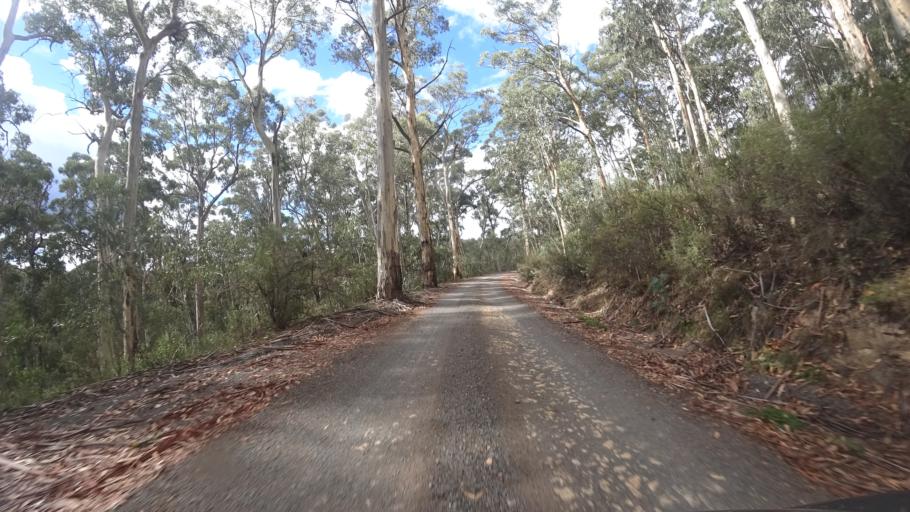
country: AU
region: New South Wales
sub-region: Tumut Shire
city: Tumut
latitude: -35.7242
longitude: 148.5054
